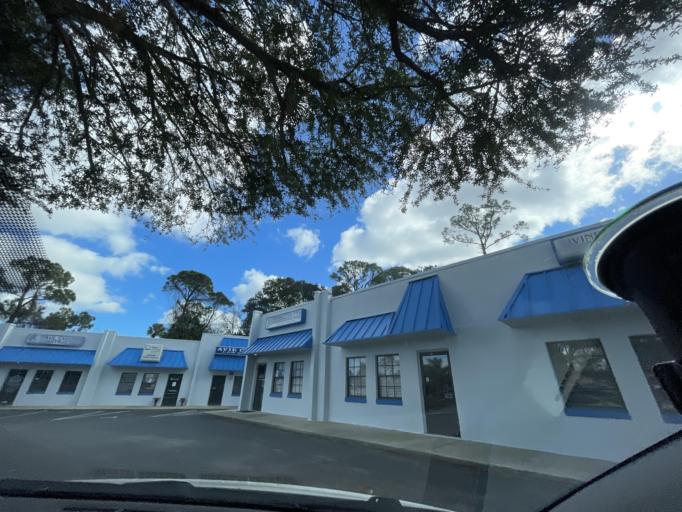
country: US
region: Florida
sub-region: Volusia County
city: South Daytona
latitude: 29.1717
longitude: -81.0357
